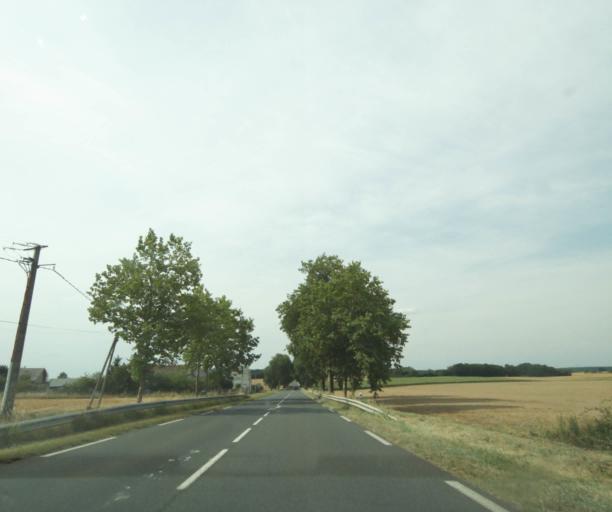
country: FR
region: Centre
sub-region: Departement d'Indre-et-Loire
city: Saint-Christophe-sur-le-Nais
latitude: 47.6380
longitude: 0.5001
